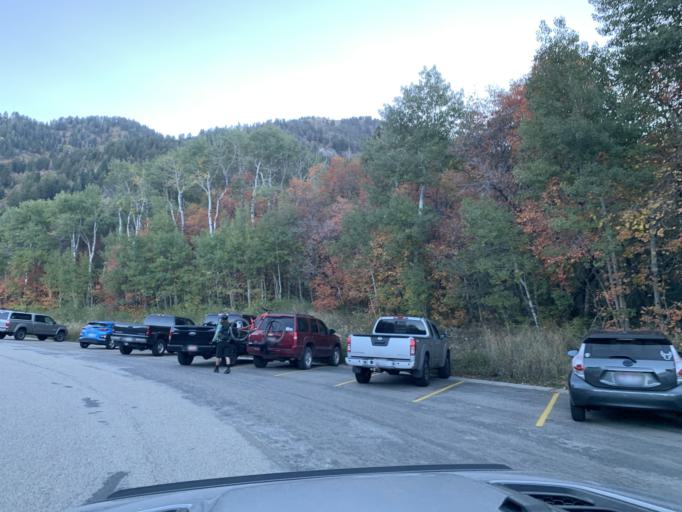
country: US
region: Utah
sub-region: Weber County
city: Uintah
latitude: 41.2184
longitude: -111.8631
